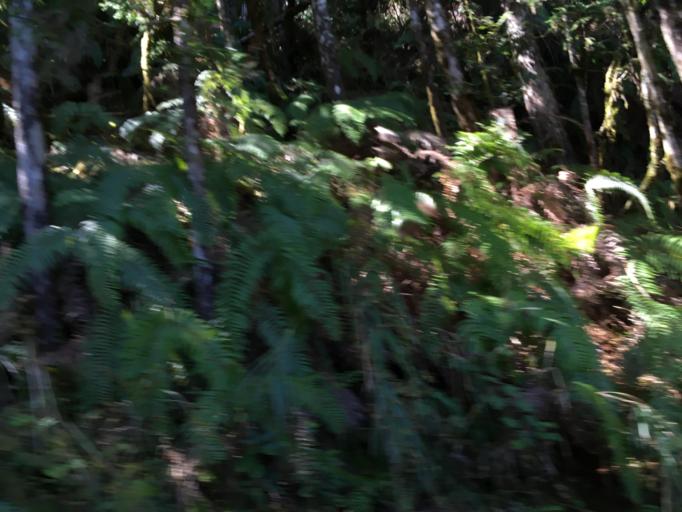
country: TW
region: Taiwan
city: Daxi
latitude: 24.5321
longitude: 121.4006
